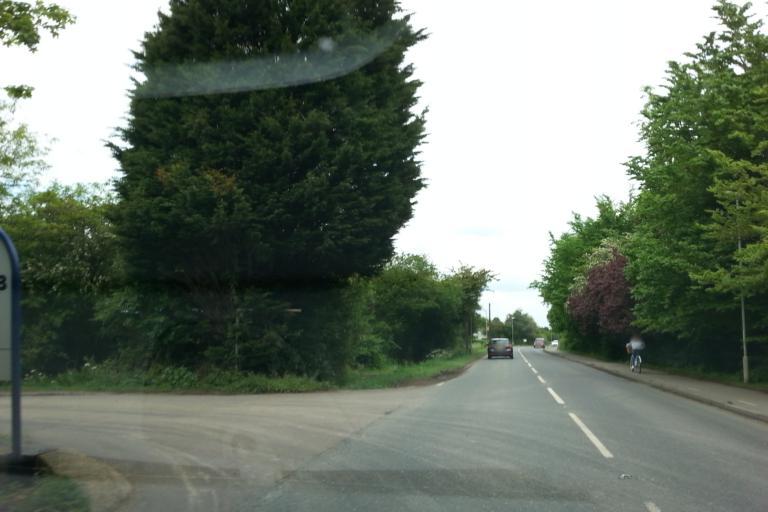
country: GB
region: England
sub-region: Cambridgeshire
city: Swavesey
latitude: 52.2966
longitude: 0.0502
